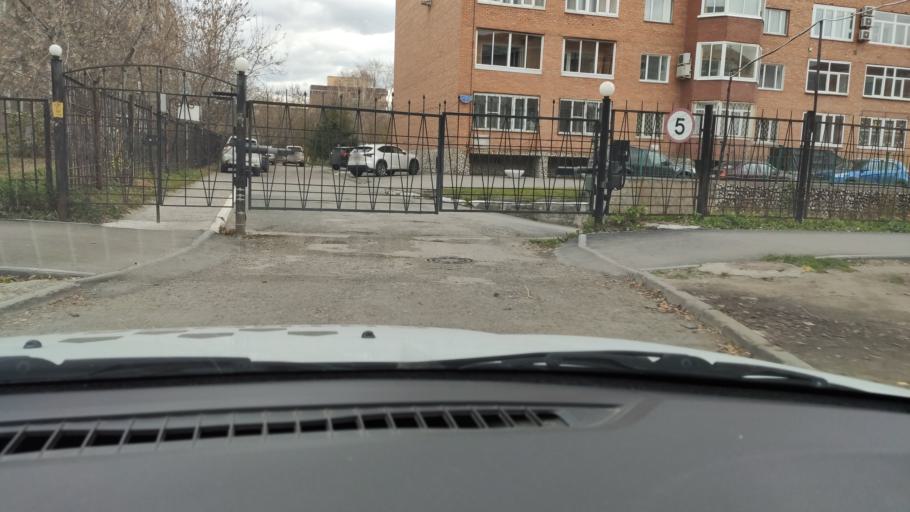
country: RU
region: Perm
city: Perm
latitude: 58.0096
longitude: 56.2036
